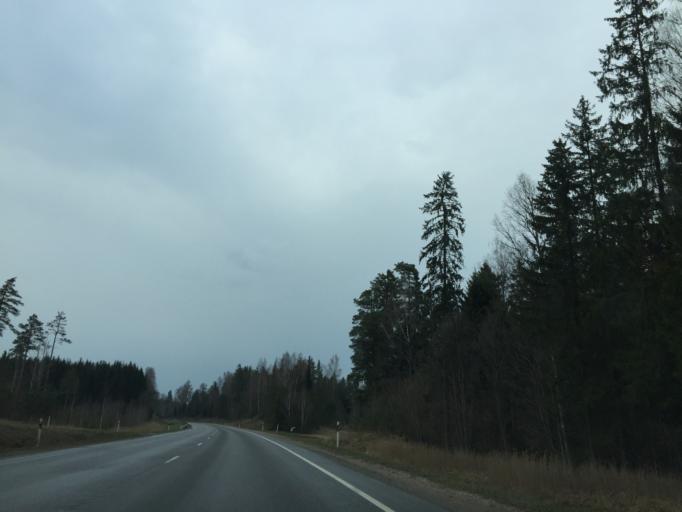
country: EE
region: Tartu
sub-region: UElenurme vald
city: Ulenurme
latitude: 58.1238
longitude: 26.7309
